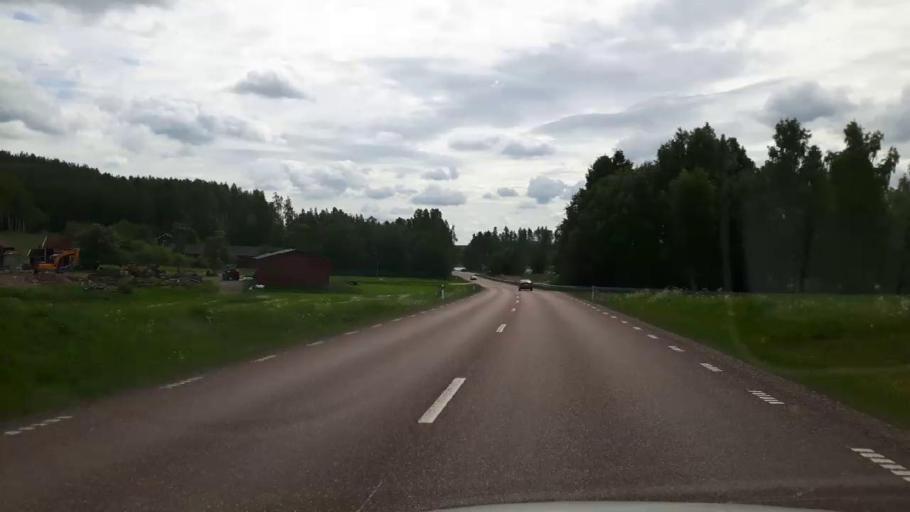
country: SE
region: Dalarna
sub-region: Hedemora Kommun
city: Hedemora
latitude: 60.3263
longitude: 15.9508
